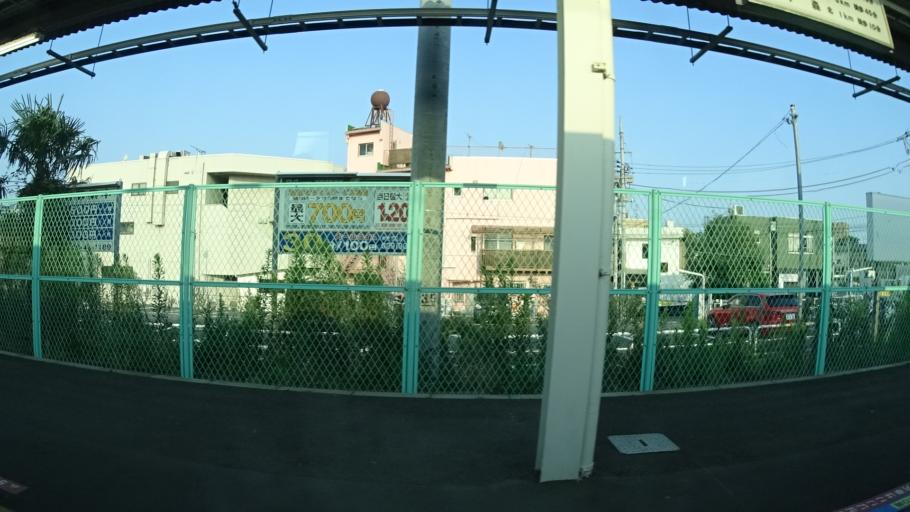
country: JP
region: Ibaraki
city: Funaishikawa
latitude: 36.5136
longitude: 140.6200
